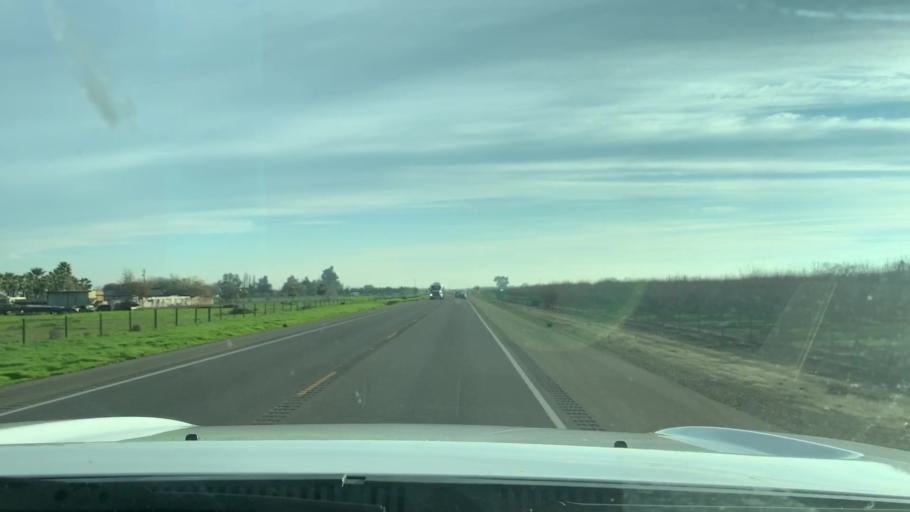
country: US
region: California
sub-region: Fresno County
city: Riverdale
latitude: 36.4190
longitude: -119.8037
